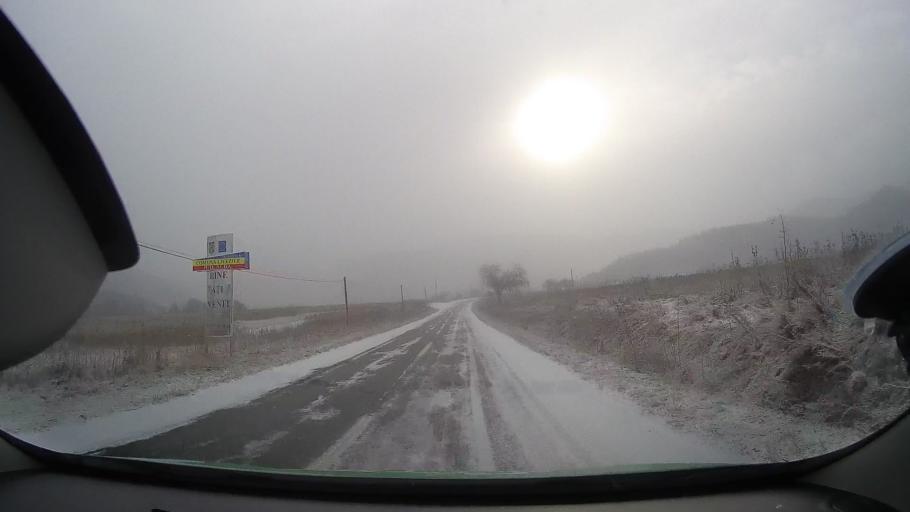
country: RO
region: Alba
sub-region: Comuna Rimetea
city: Rimetea
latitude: 46.3992
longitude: 23.5592
